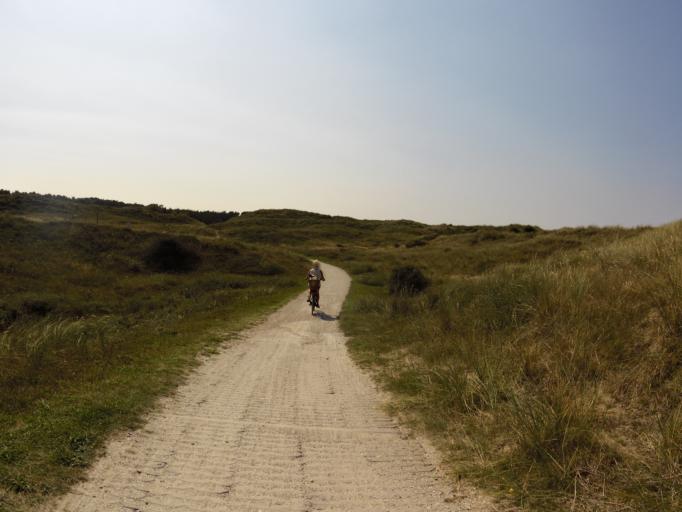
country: NL
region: North Holland
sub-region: Gemeente Schagen
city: Harenkarspel
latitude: 52.7819
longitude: 4.6712
